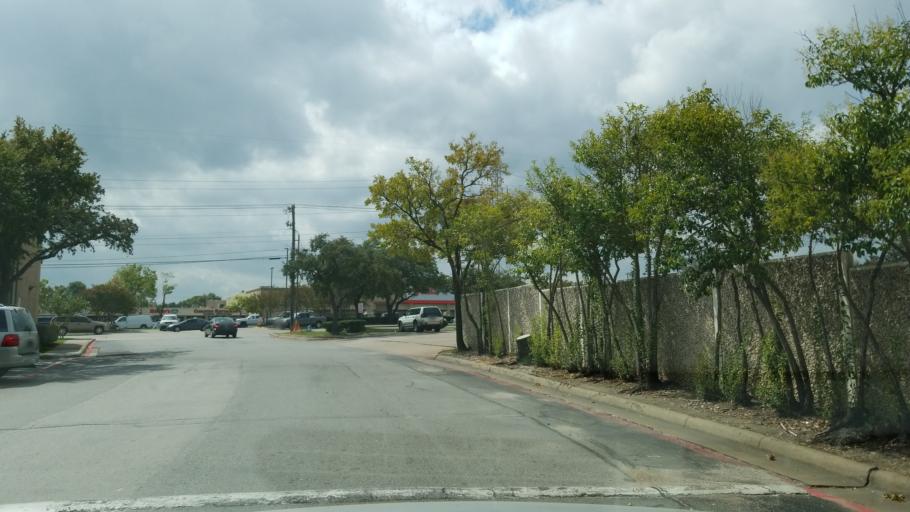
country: US
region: Texas
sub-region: Dallas County
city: Richardson
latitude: 32.9406
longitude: -96.7663
